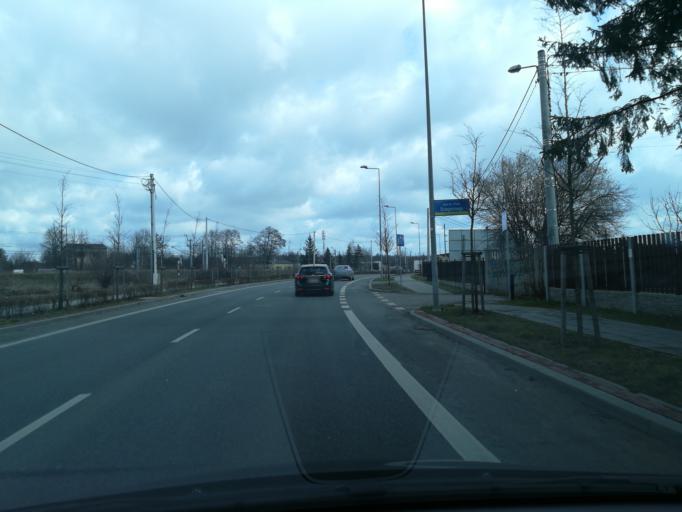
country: PL
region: Silesian Voivodeship
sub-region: Czestochowa
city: Czestochowa
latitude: 50.8274
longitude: 19.1366
